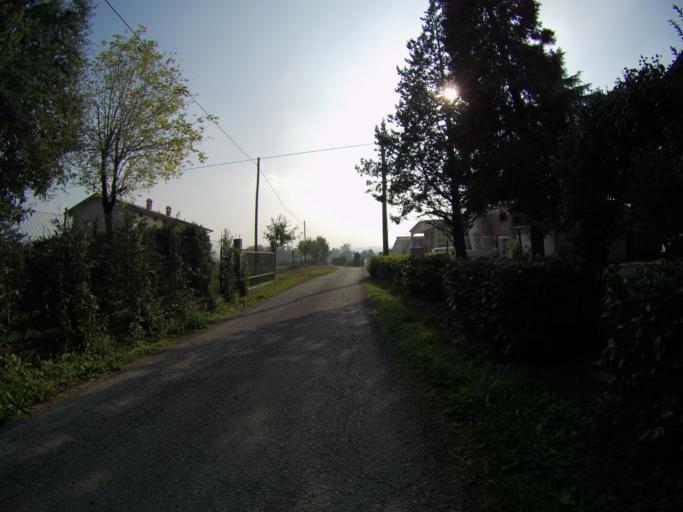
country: IT
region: Emilia-Romagna
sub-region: Provincia di Reggio Emilia
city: San Bartolomeo
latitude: 44.6533
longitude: 10.5321
